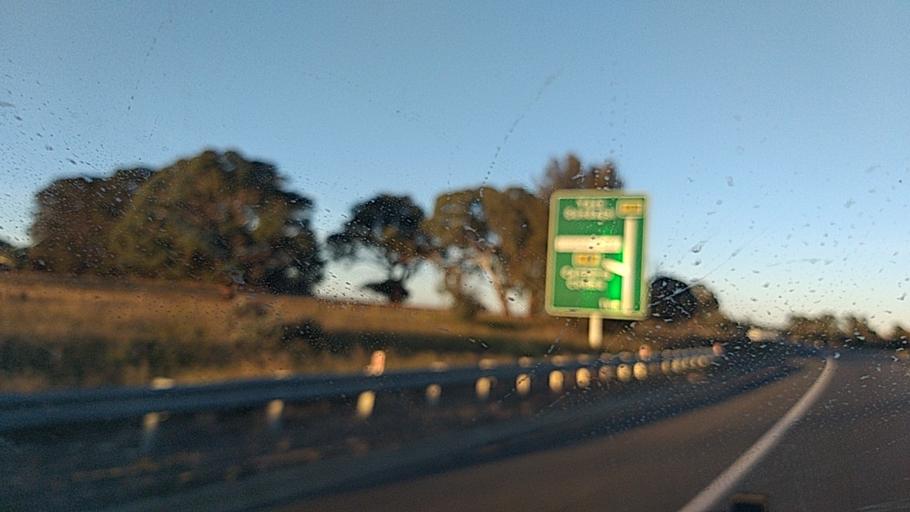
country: AU
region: New South Wales
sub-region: Goulburn Mulwaree
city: Goulburn
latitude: -34.7895
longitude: 149.6228
